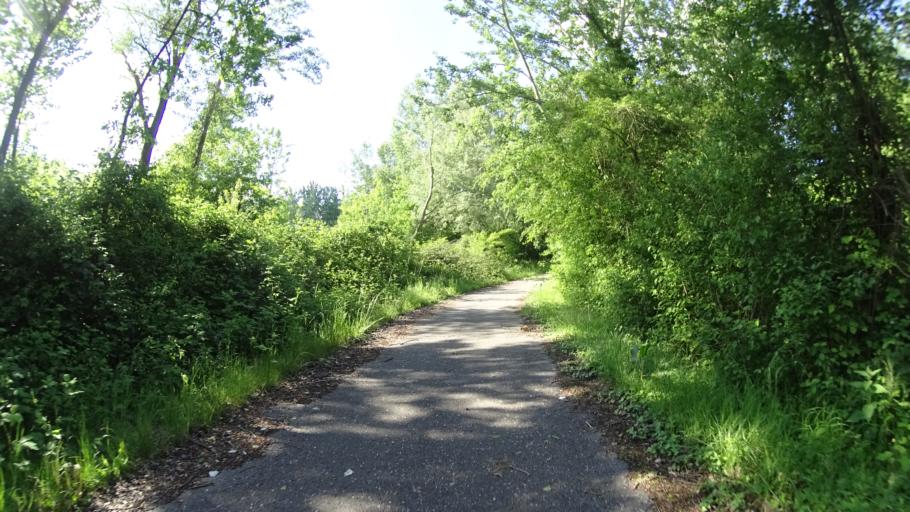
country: DE
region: Rheinland-Pfalz
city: Neupotz
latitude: 49.0655
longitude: 8.3440
